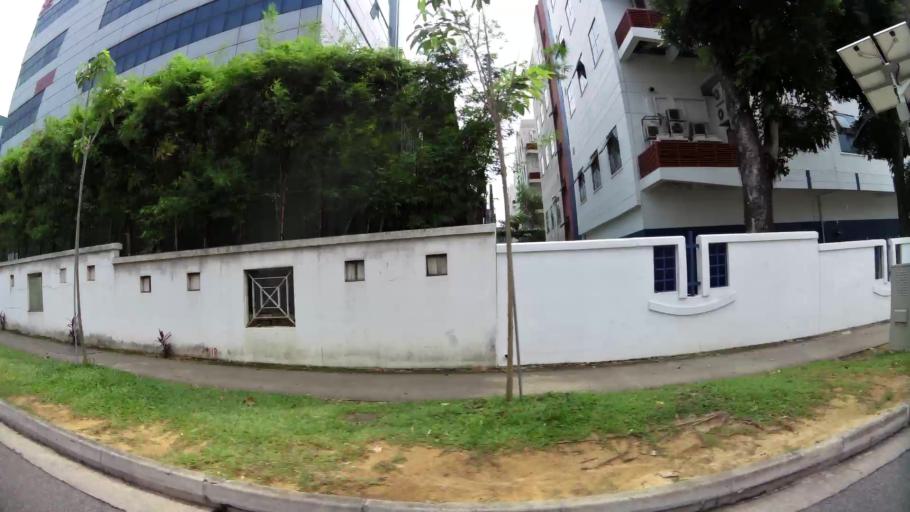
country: SG
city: Singapore
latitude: 1.3367
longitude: 103.9065
